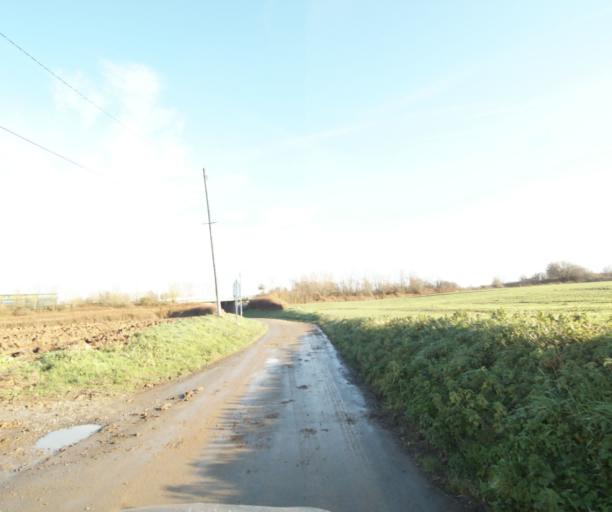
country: FR
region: Nord-Pas-de-Calais
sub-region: Departement du Nord
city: Saultain
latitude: 50.3358
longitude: 3.5872
